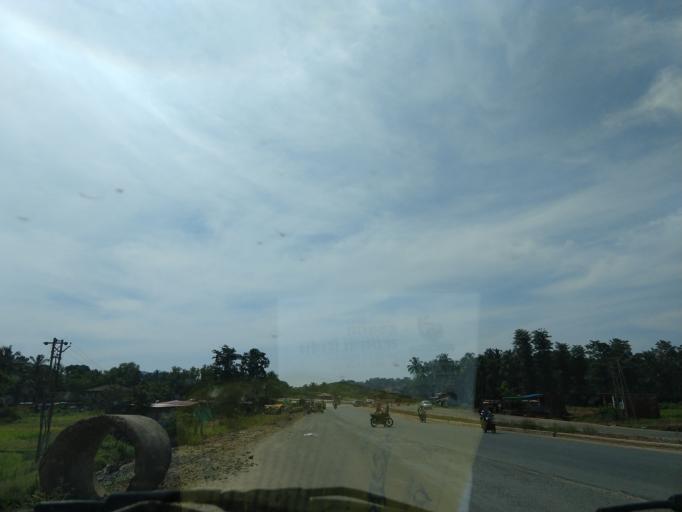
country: IN
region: Maharashtra
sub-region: Sindhudurg
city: Kudal
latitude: 15.9523
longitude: 73.7389
